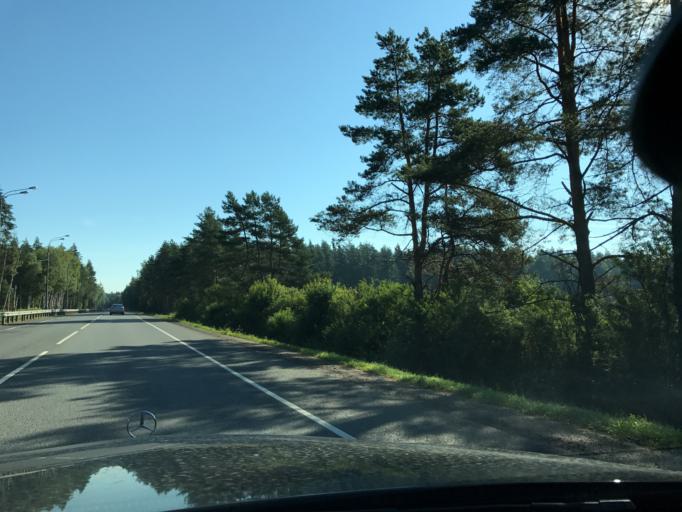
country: RU
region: Moskovskaya
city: Chernogolovka
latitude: 55.9665
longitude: 38.2858
